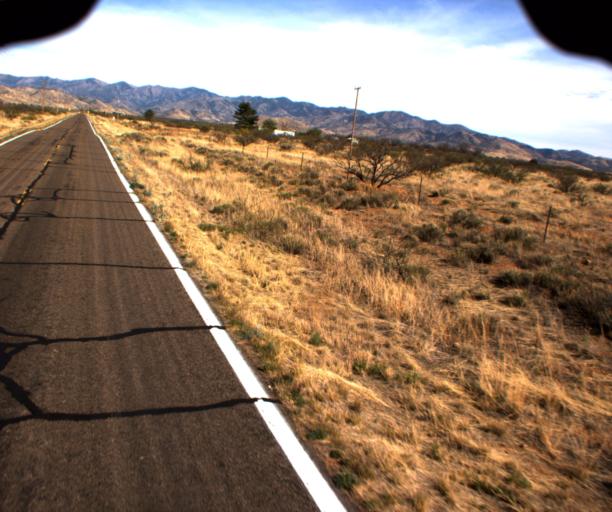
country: US
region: Arizona
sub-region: Cochise County
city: Willcox
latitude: 31.8760
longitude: -109.4997
